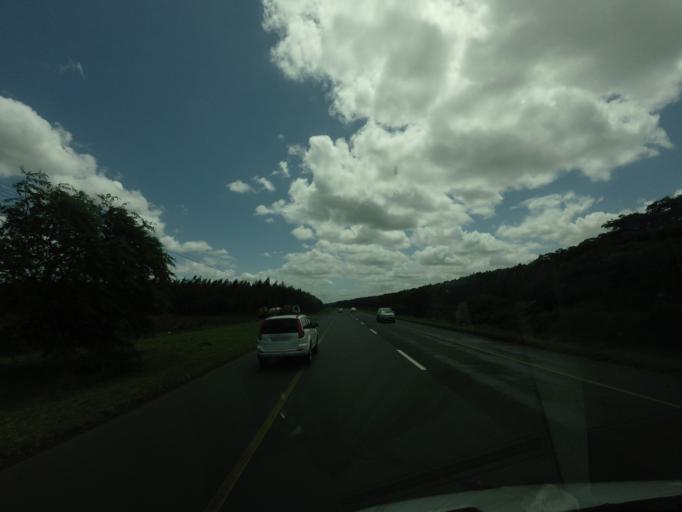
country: ZA
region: KwaZulu-Natal
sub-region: uThungulu District Municipality
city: KwaMbonambi
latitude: -28.5647
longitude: 32.1141
